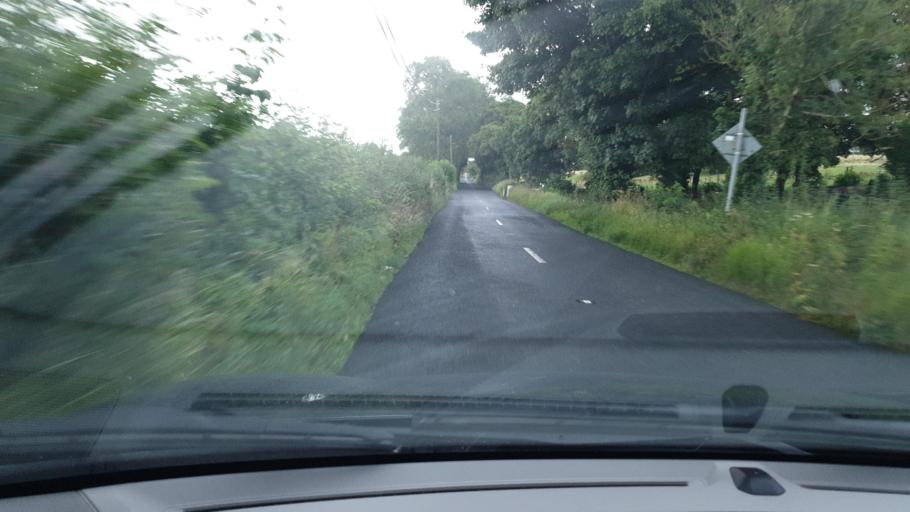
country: IE
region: Leinster
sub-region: South Dublin
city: Rathcoole
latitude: 53.2626
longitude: -6.4943
